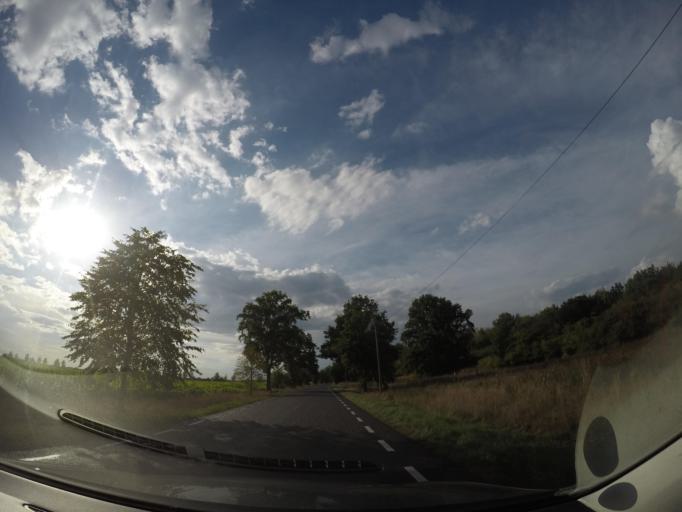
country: DE
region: Saxony-Anhalt
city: Mieste
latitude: 52.5179
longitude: 11.1520
